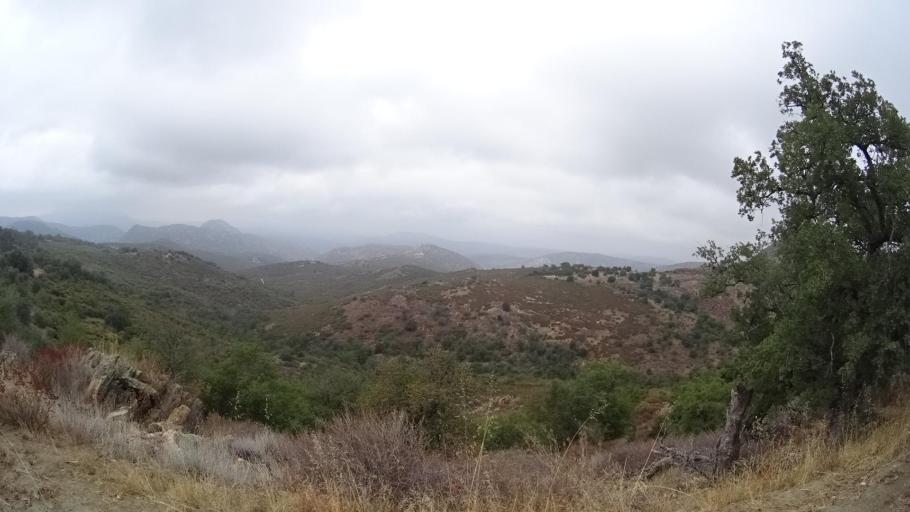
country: US
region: California
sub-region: San Diego County
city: Julian
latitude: 32.9910
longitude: -116.6571
